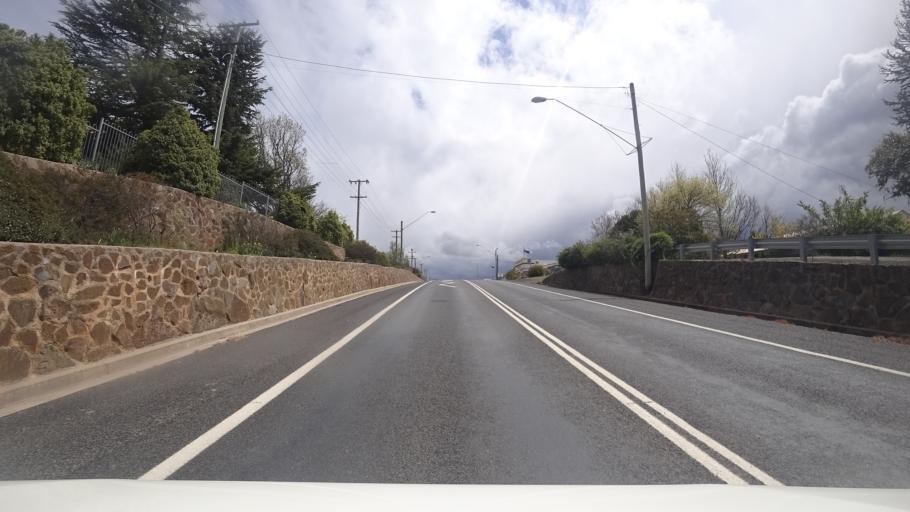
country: AU
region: New South Wales
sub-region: Oberon
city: Oberon
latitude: -33.7051
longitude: 149.8643
